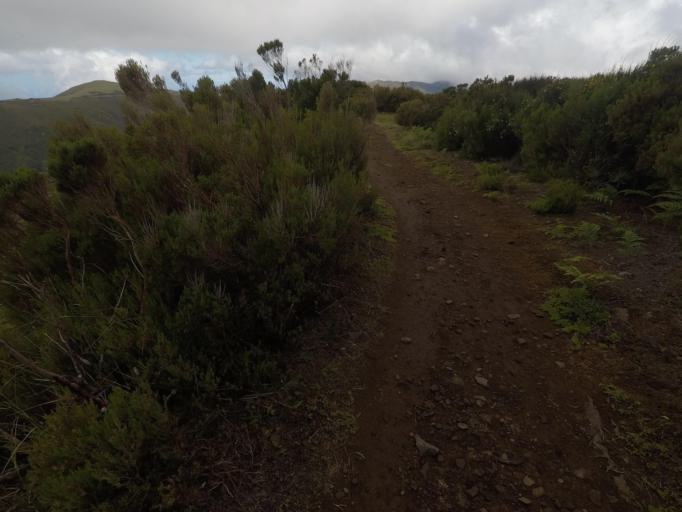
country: PT
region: Madeira
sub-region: Calheta
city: Arco da Calheta
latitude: 32.7732
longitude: -17.1314
